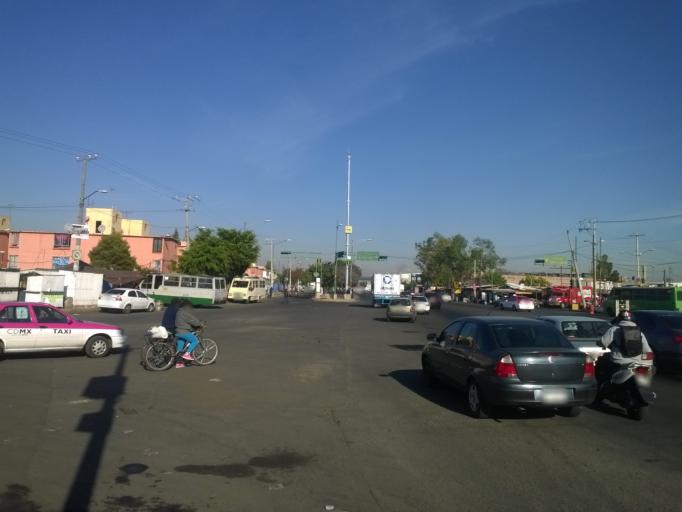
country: MX
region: Mexico City
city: Iztapalapa
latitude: 19.3738
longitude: -99.0521
